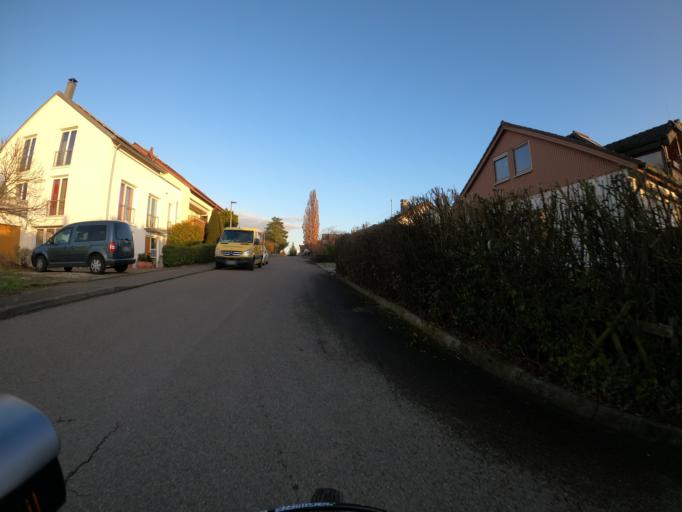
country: DE
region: Baden-Wuerttemberg
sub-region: Regierungsbezirk Stuttgart
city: Notzingen
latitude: 48.6738
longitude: 9.4512
